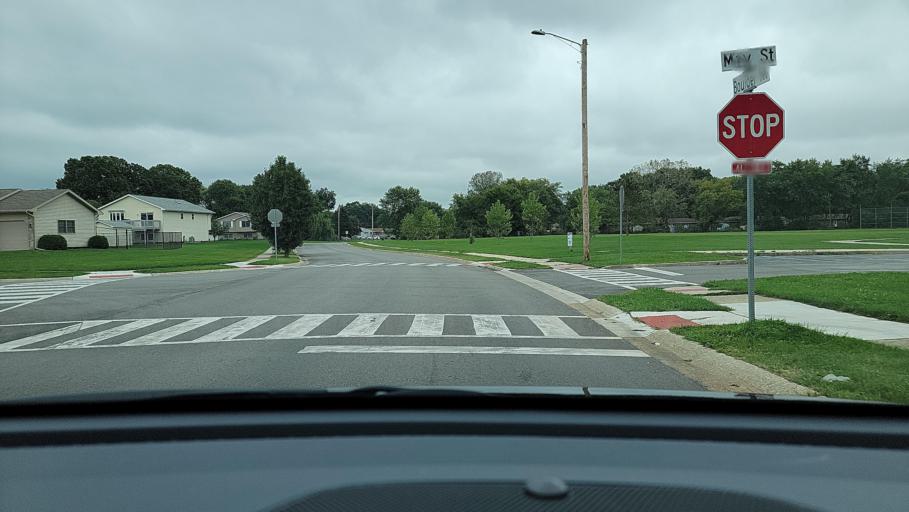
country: US
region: Indiana
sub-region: Lake County
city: Lake Station
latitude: 41.5570
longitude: -87.2116
